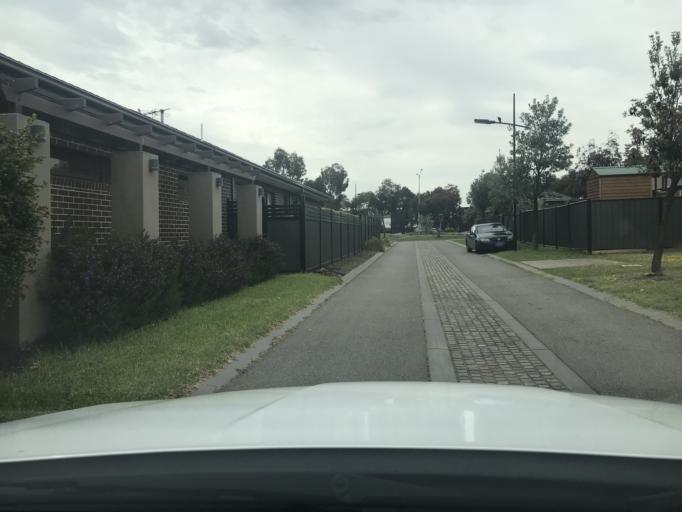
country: AU
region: Victoria
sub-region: Hume
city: Roxburgh Park
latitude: -37.5941
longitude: 144.9044
